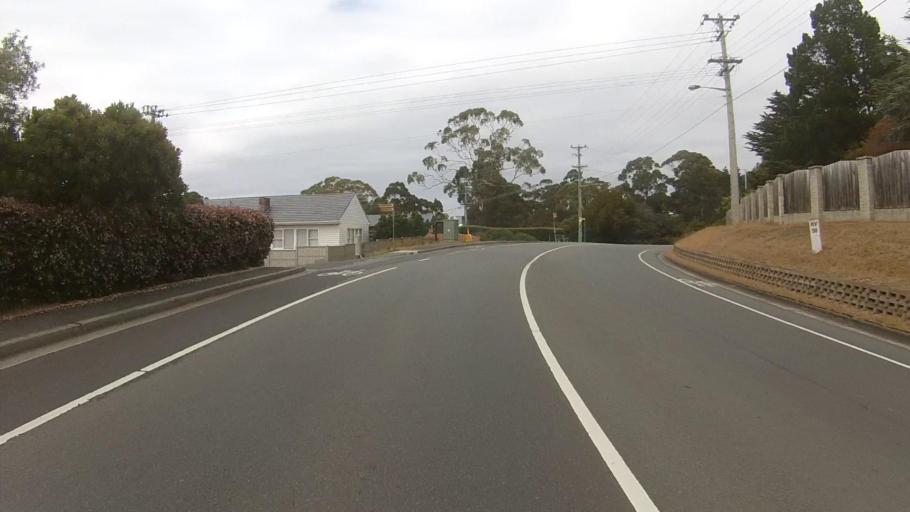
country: AU
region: Tasmania
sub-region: Kingborough
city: Taroona
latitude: -42.9360
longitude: 147.3544
